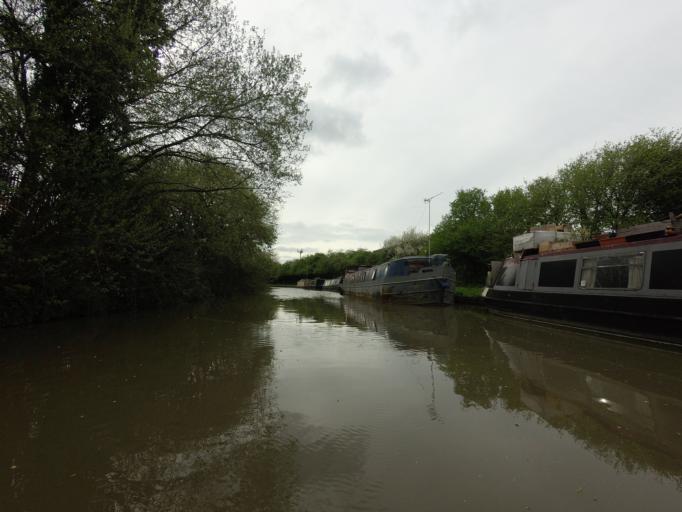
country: GB
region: England
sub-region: Milton Keynes
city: Bradwell
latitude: 52.0649
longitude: -0.8159
